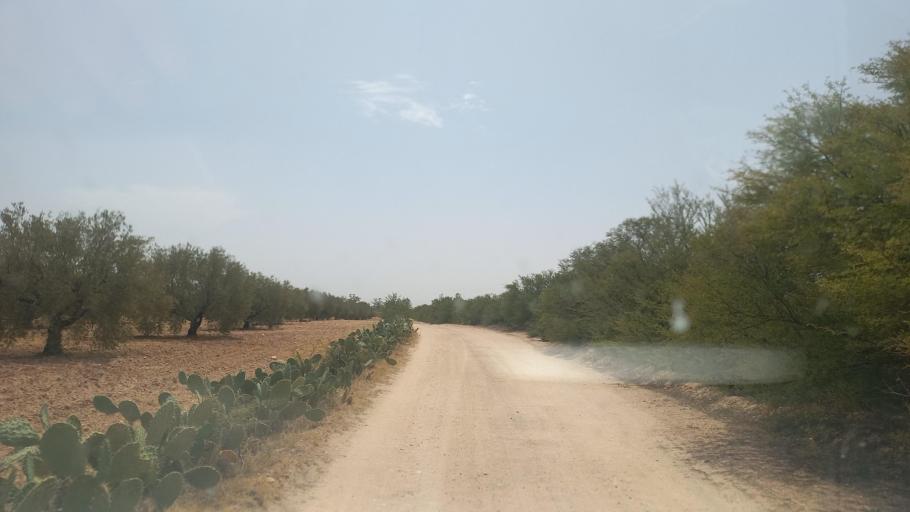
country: TN
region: Al Qasrayn
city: Kasserine
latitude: 35.2554
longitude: 9.0066
